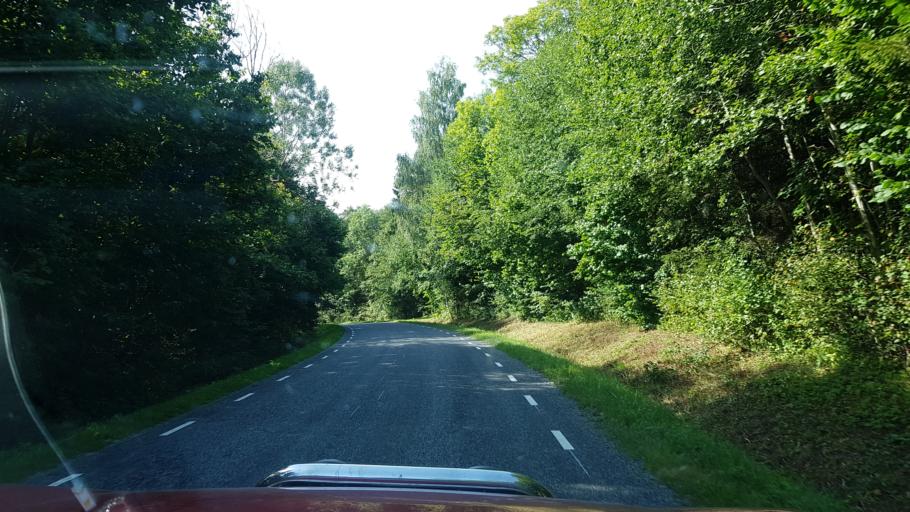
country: EE
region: Viljandimaa
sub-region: Viljandi linn
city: Viljandi
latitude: 58.3234
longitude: 25.5320
